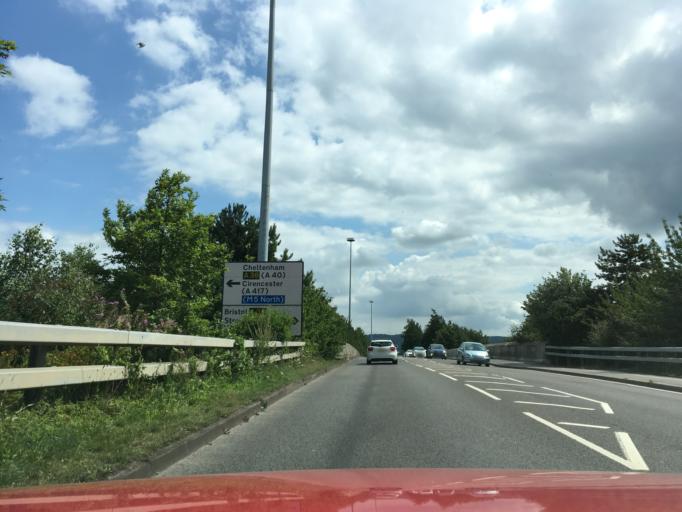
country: GB
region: England
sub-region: Gloucestershire
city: Gloucester
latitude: 51.8597
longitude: -2.2240
